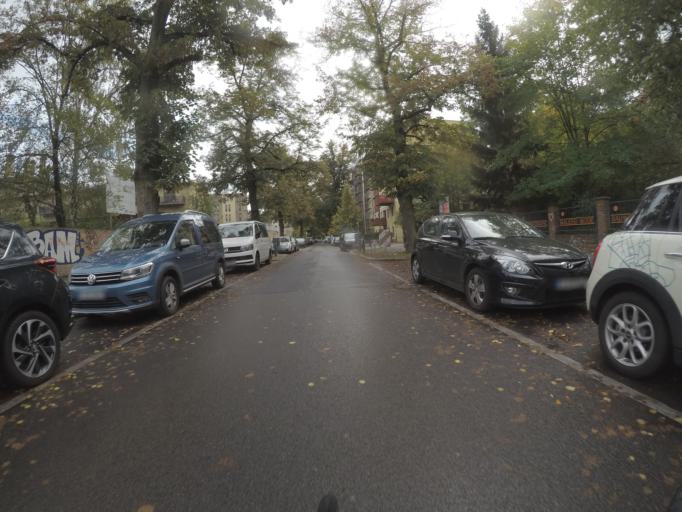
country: DE
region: Berlin
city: Pankow
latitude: 52.5677
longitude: 13.4021
